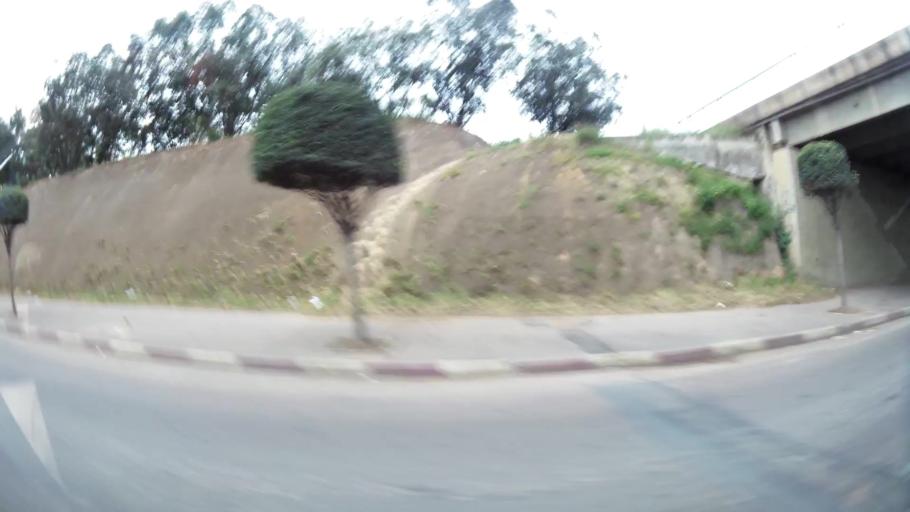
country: MA
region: Grand Casablanca
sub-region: Casablanca
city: Casablanca
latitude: 33.5304
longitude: -7.6374
